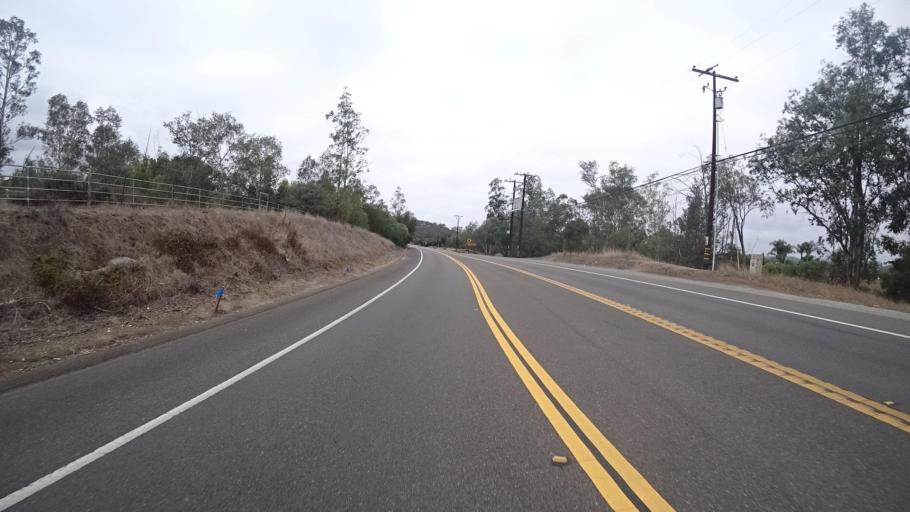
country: US
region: California
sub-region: San Diego County
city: Ramona
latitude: 33.0657
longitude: -116.8741
